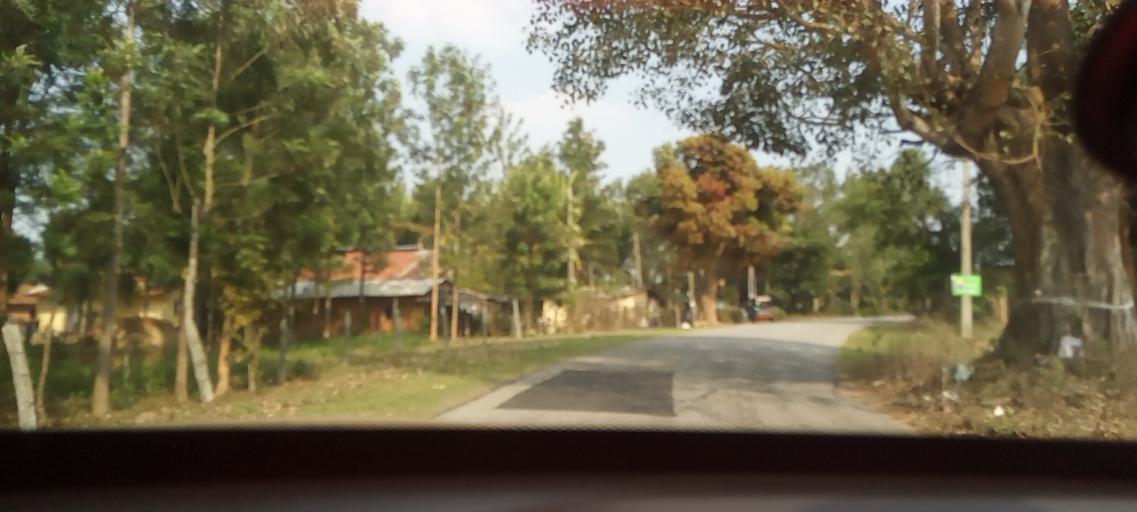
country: IN
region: Karnataka
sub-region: Hassan
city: Belur
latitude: 13.1836
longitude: 75.8361
